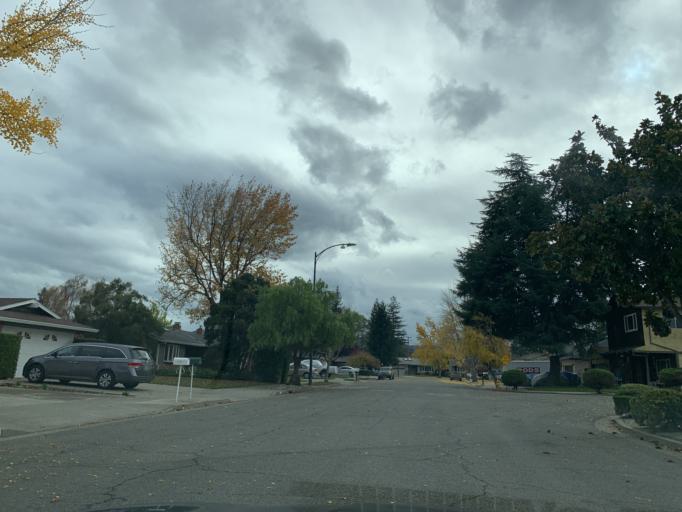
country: US
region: California
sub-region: Santa Clara County
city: Campbell
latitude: 37.2705
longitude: -121.9776
